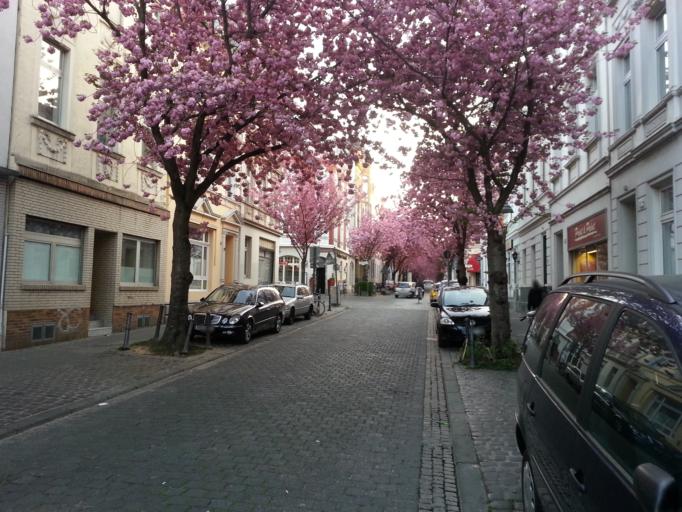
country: DE
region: North Rhine-Westphalia
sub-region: Regierungsbezirk Koln
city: Bonn
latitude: 50.7395
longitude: 7.0924
